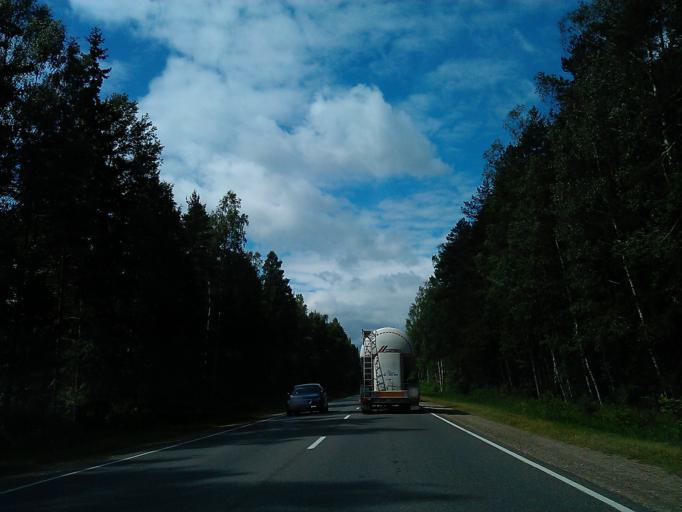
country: LV
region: Engure
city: Smarde
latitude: 56.9177
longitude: 23.3835
